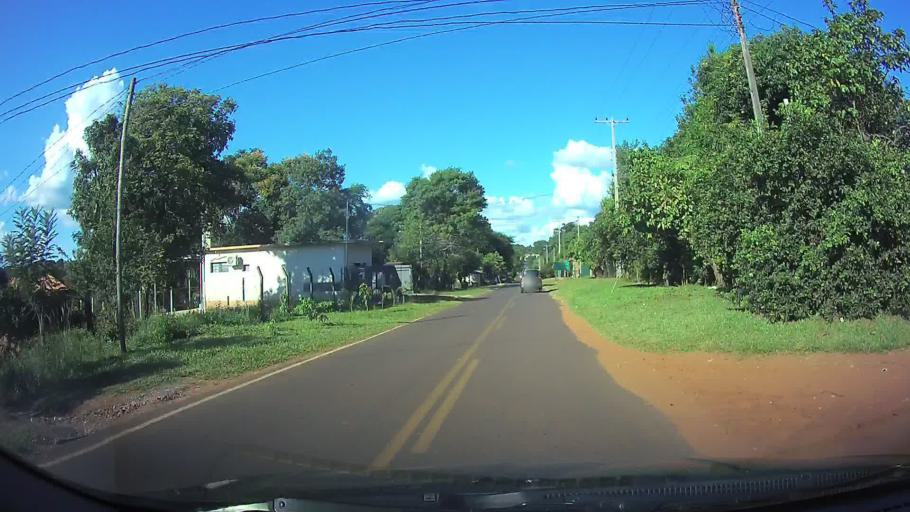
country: PY
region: Central
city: Aregua
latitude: -25.3444
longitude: -57.3892
